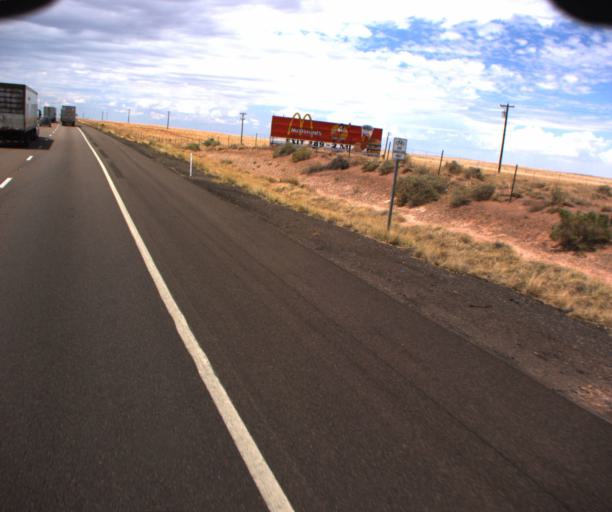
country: US
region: Arizona
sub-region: Navajo County
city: Holbrook
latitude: 34.9698
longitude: -110.0943
